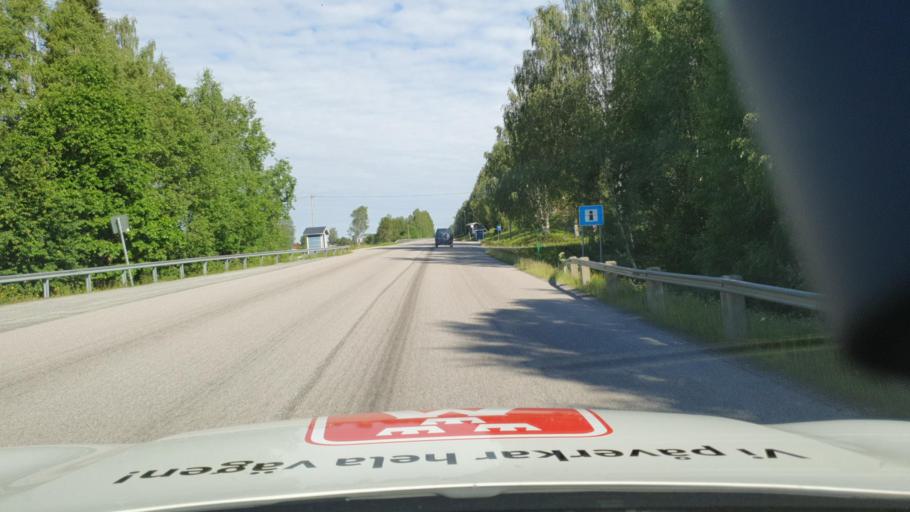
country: SE
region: Vaesterbotten
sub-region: Vannas Kommun
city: Vannasby
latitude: 64.1268
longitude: 19.9572
